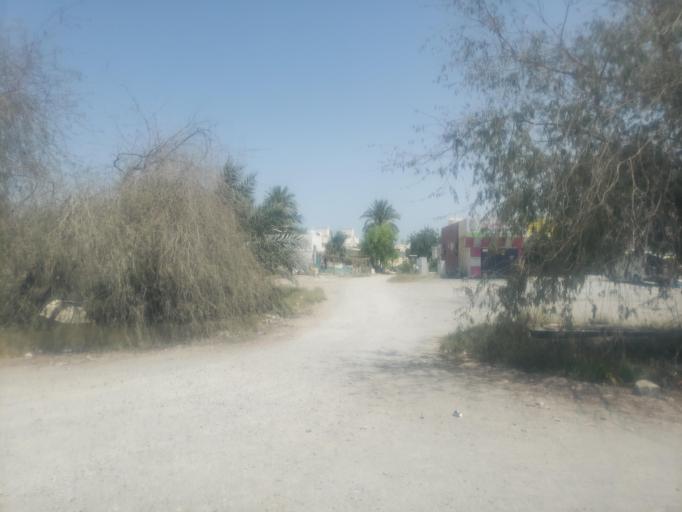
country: AE
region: Ra's al Khaymah
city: Ras al-Khaimah
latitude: 25.8046
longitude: 55.9641
